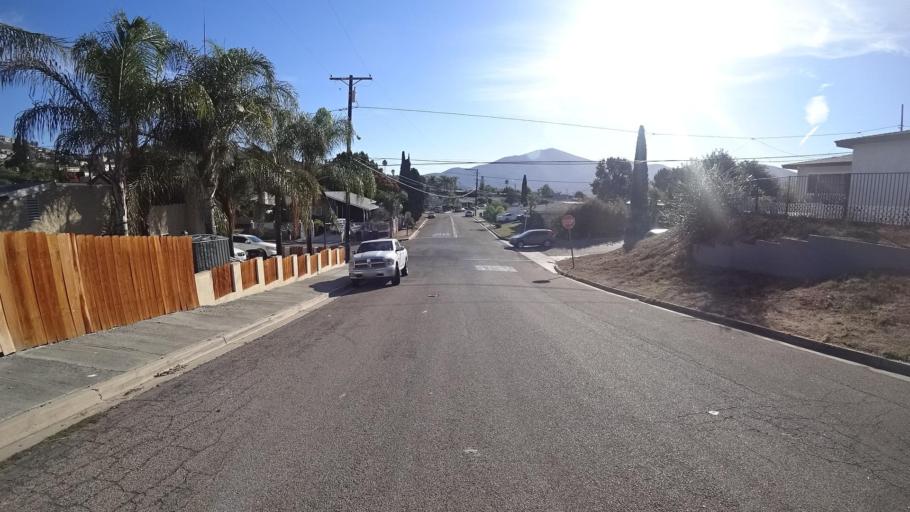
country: US
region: California
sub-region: San Diego County
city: La Presa
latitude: 32.7116
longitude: -116.9935
